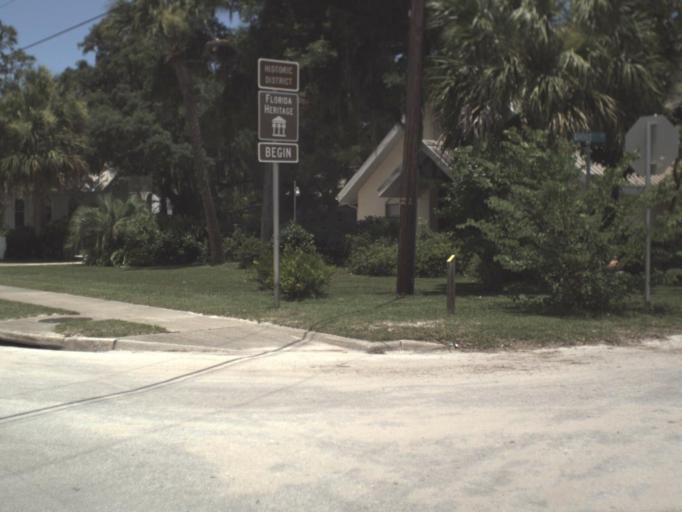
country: US
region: Florida
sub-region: Clay County
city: Keystone Heights
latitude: 29.7097
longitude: -82.0481
